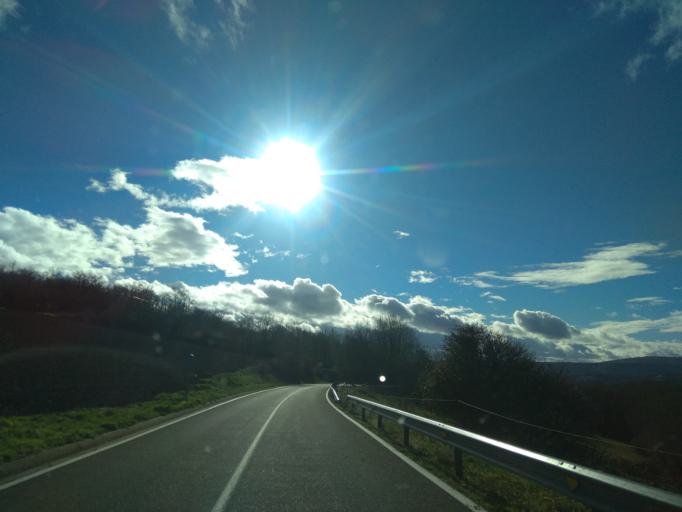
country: ES
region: Cantabria
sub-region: Provincia de Cantabria
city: San Martin de Elines
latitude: 42.9194
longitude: -3.8634
